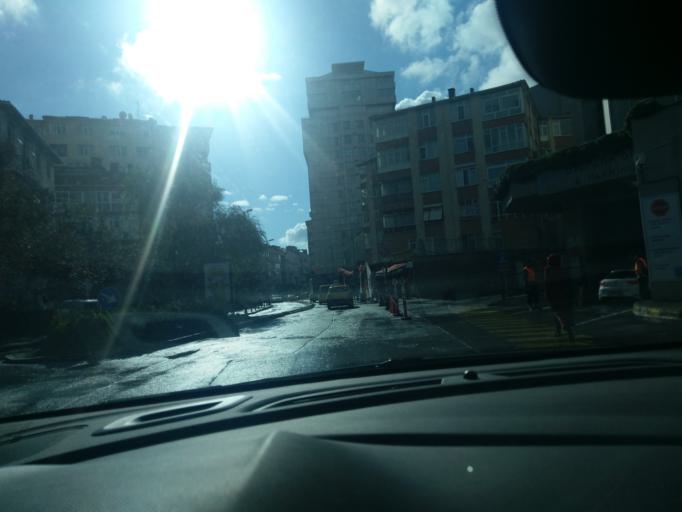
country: TR
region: Istanbul
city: Sisli
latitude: 41.0630
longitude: 28.9944
